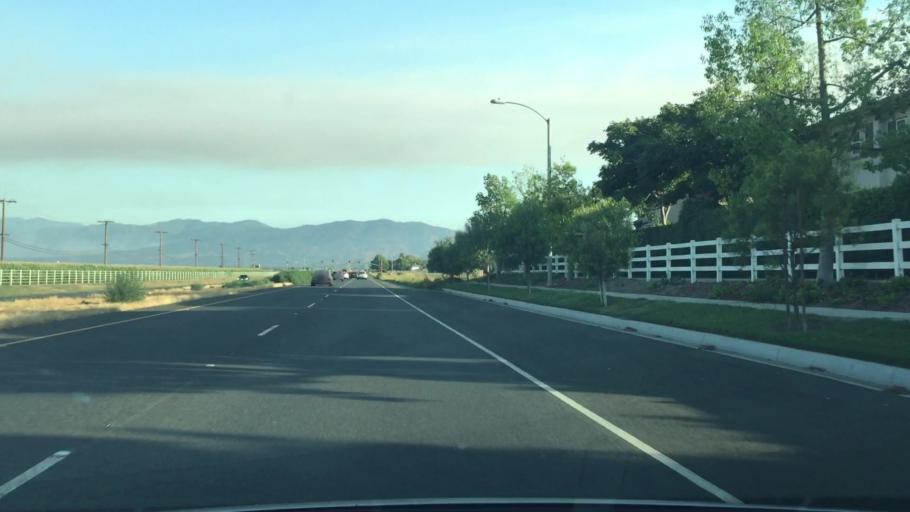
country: US
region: California
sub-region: San Bernardino County
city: Chino
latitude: 33.9871
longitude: -117.6509
